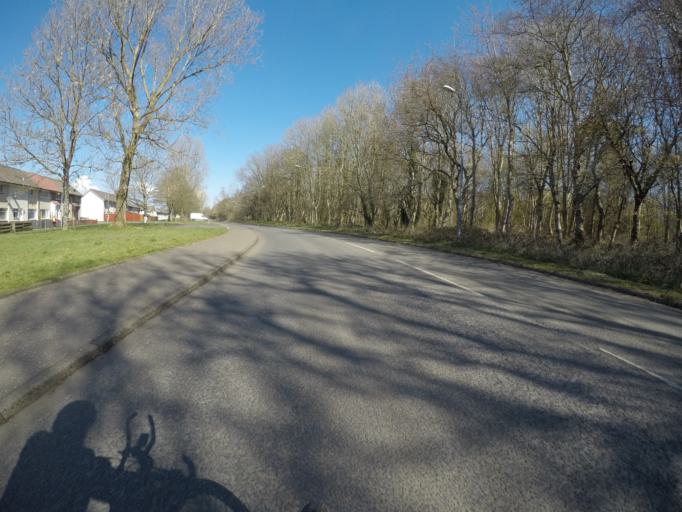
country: GB
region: Scotland
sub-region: North Ayrshire
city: Irvine
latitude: 55.6292
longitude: -4.6579
